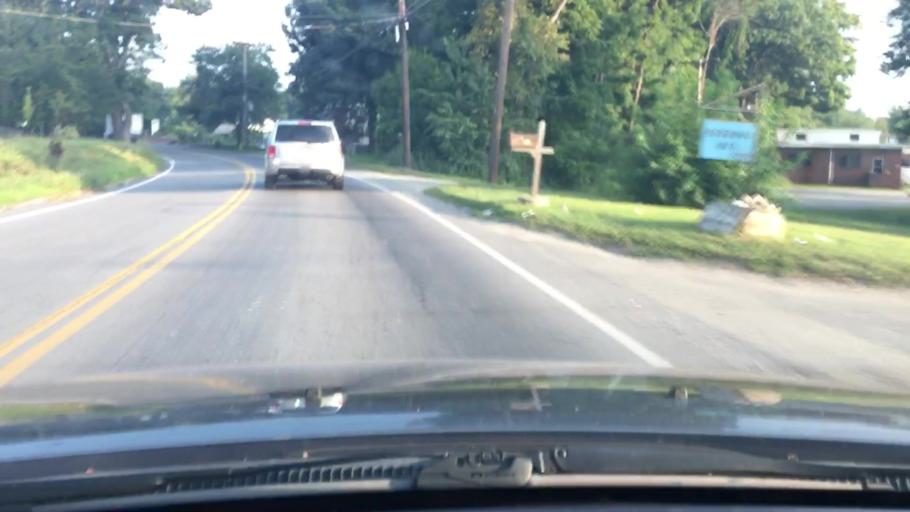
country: US
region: Massachusetts
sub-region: Worcester County
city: Westborough
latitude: 42.2557
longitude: -71.5924
